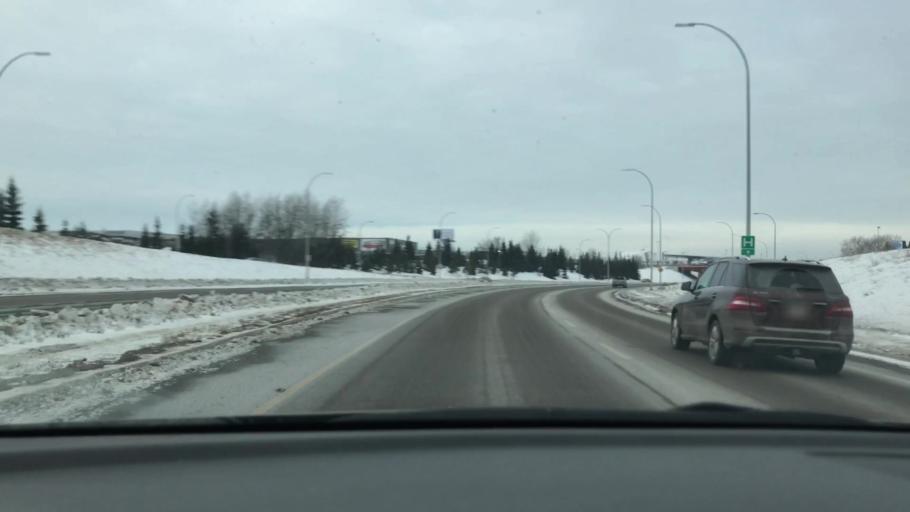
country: CA
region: Alberta
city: Edmonton
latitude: 53.5143
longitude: -113.4192
